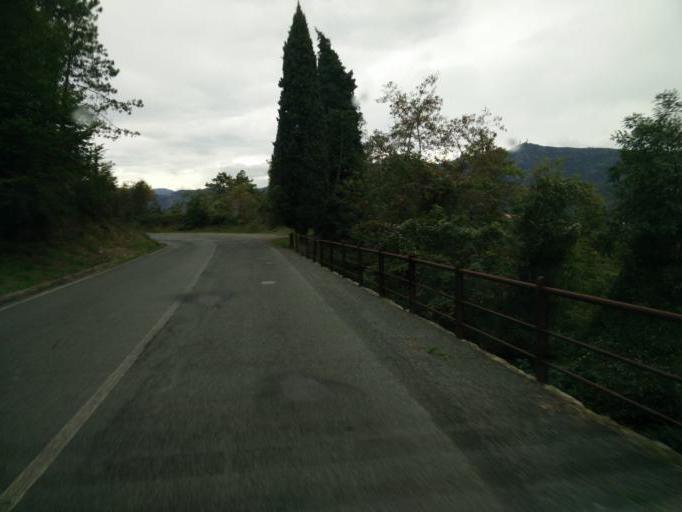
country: IT
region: Liguria
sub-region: Provincia di La Spezia
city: Framura
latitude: 44.2144
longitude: 9.5600
